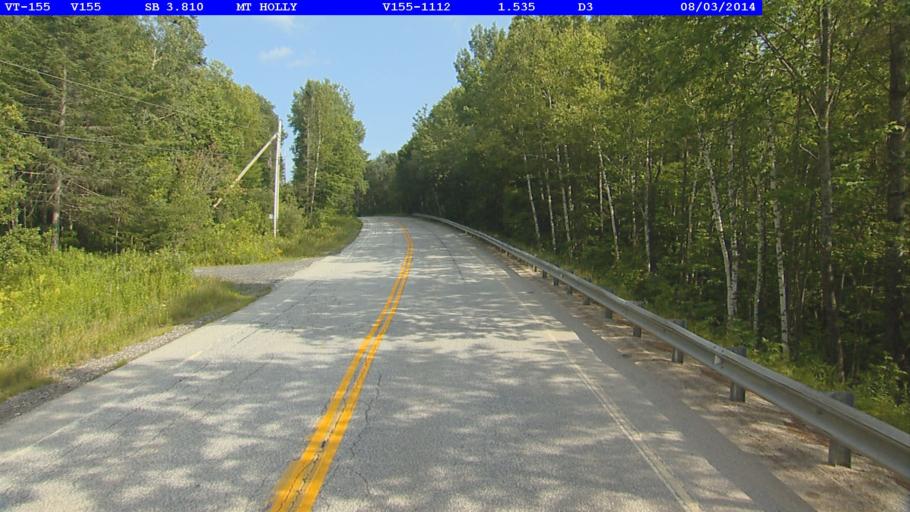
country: US
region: Vermont
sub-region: Windsor County
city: Chester
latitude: 43.3835
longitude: -72.8013
